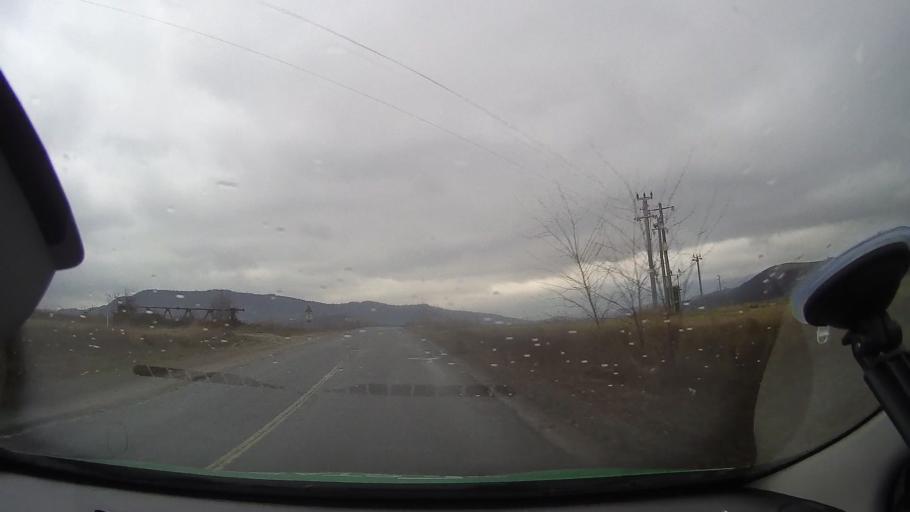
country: RO
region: Arad
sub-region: Comuna Halmagiu
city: Halmagiu
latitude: 46.2334
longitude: 22.5584
